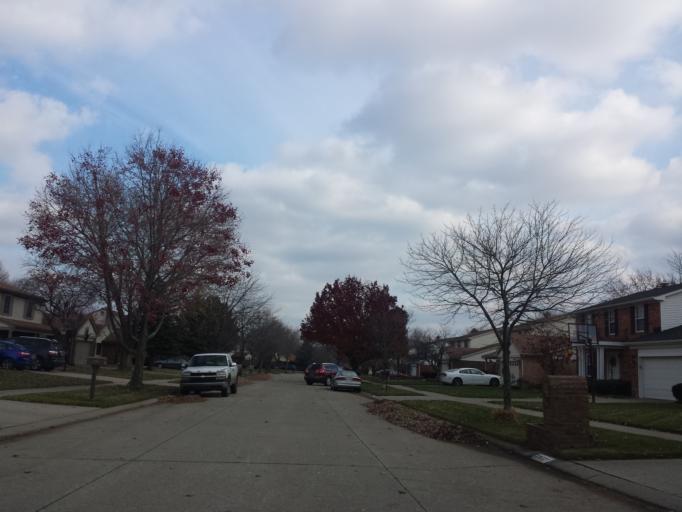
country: US
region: Michigan
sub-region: Wayne County
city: Plymouth
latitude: 42.4065
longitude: -83.4305
